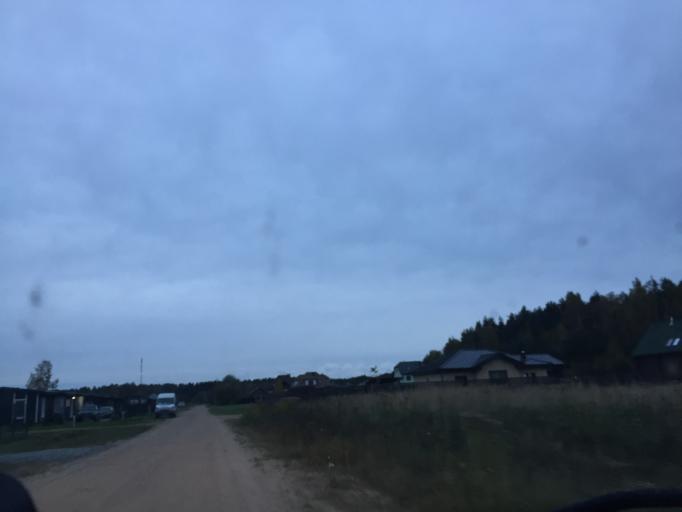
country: LV
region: Adazi
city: Adazi
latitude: 57.0846
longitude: 24.3781
